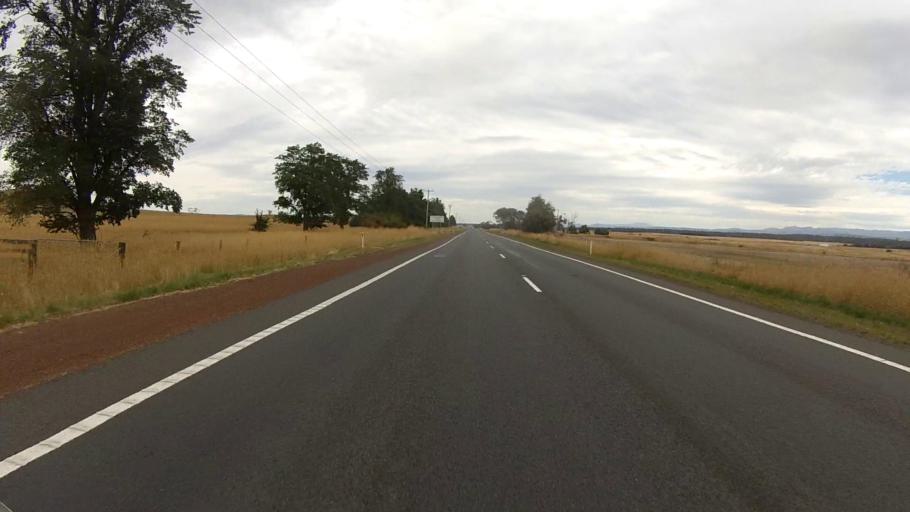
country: AU
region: Tasmania
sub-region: Northern Midlands
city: Evandale
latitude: -41.9032
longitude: 147.4775
